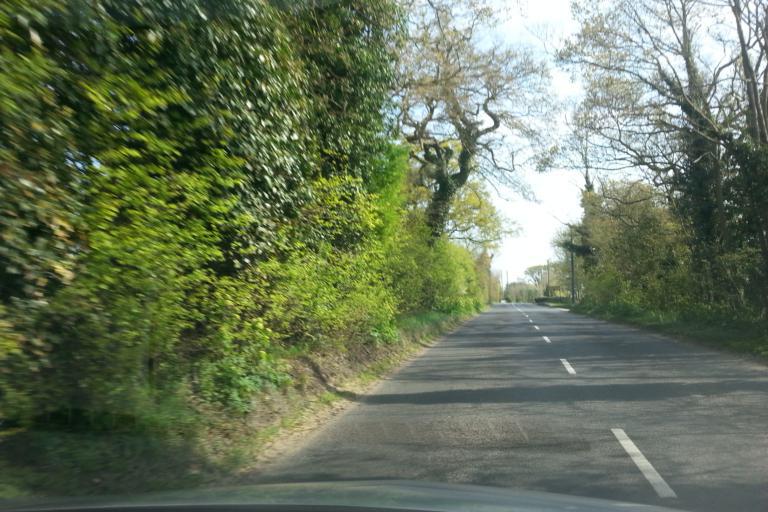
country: GB
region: England
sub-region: Suffolk
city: Wickham Market
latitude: 52.1114
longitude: 1.3758
